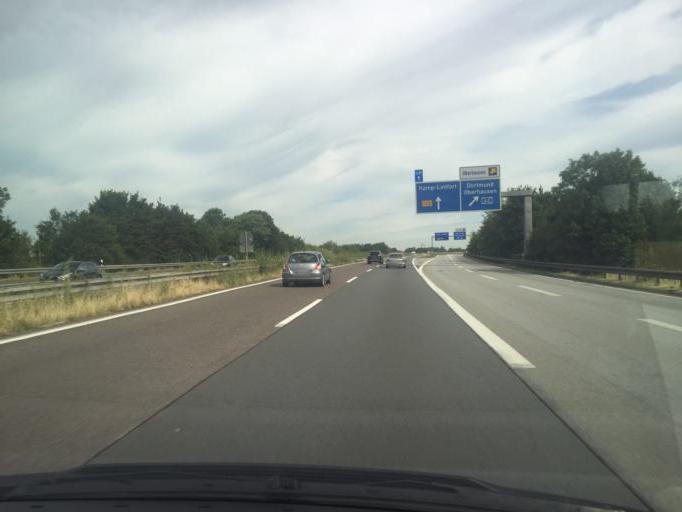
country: DE
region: North Rhine-Westphalia
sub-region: Regierungsbezirk Dusseldorf
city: Kamp-Lintfort
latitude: 51.4841
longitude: 6.5791
